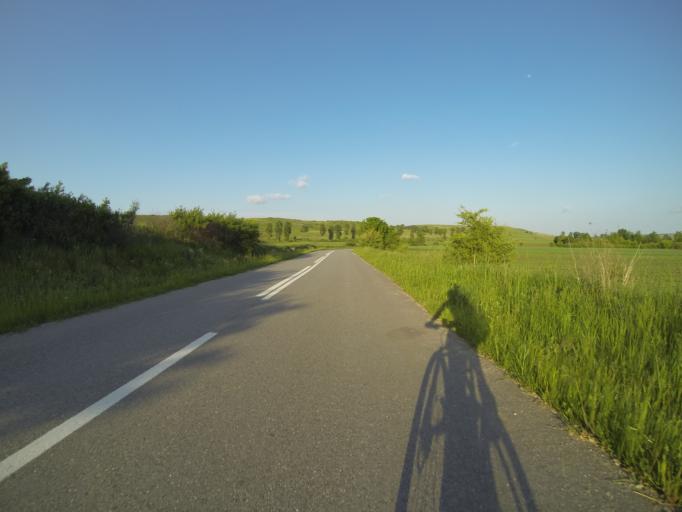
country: RO
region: Dolj
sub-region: Comuna Salcuta
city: Salcuta
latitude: 44.2641
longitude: 23.4435
